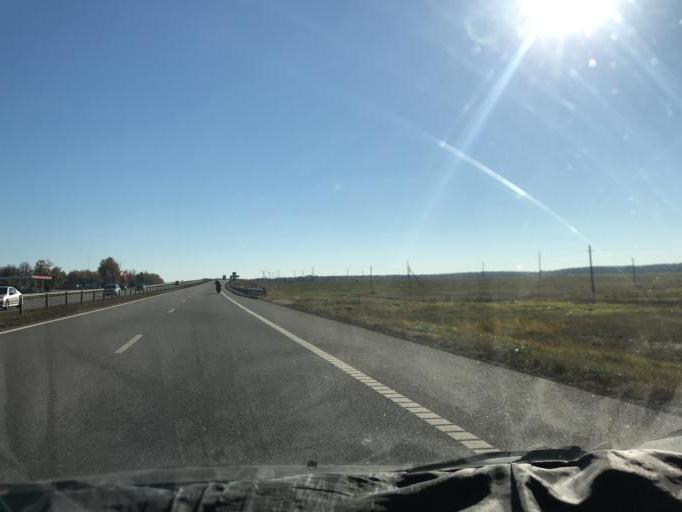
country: BY
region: Mogilev
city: Yalizava
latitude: 53.2191
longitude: 29.0275
